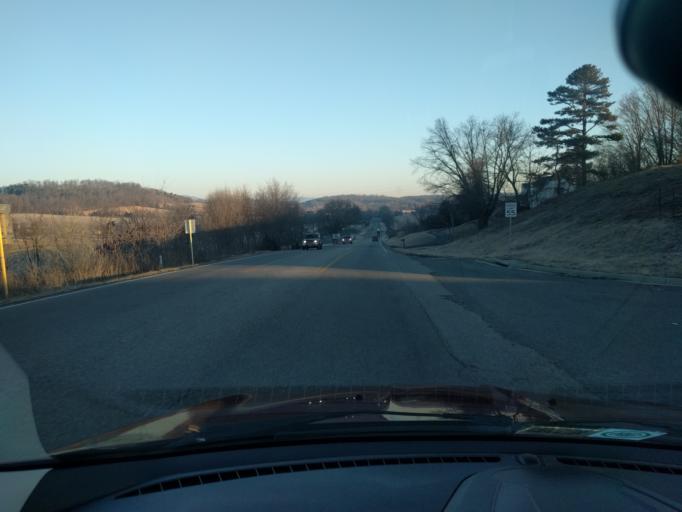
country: US
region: Virginia
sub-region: Augusta County
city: Weyers Cave
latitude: 38.2907
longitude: -78.9356
